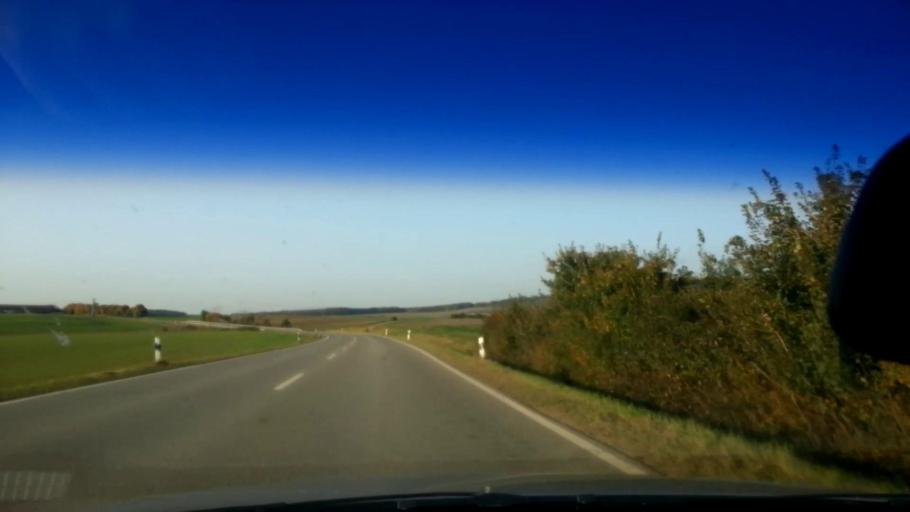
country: DE
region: Bavaria
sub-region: Upper Franconia
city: Schesslitz
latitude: 49.9945
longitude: 11.0239
